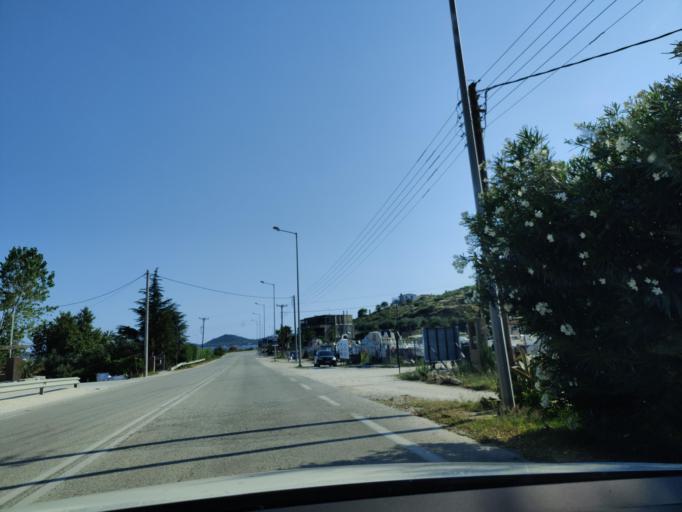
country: GR
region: East Macedonia and Thrace
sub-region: Nomos Kavalas
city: Nea Iraklitsa
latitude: 40.8524
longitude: 24.3135
